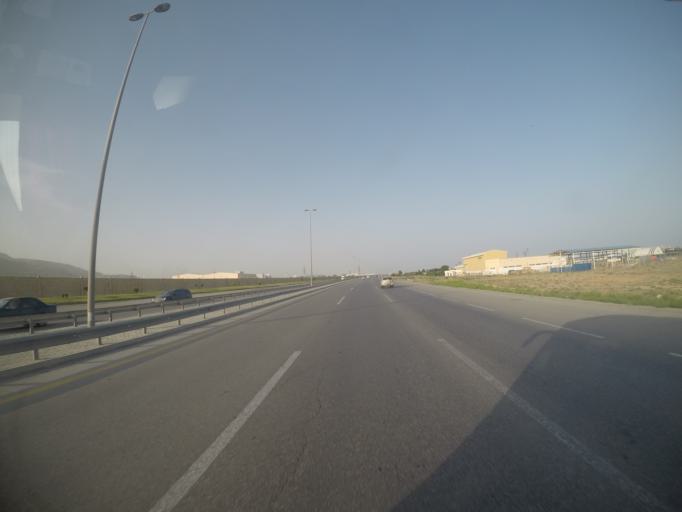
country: AZ
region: Baki
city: Puta
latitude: 40.2588
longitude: 49.6375
